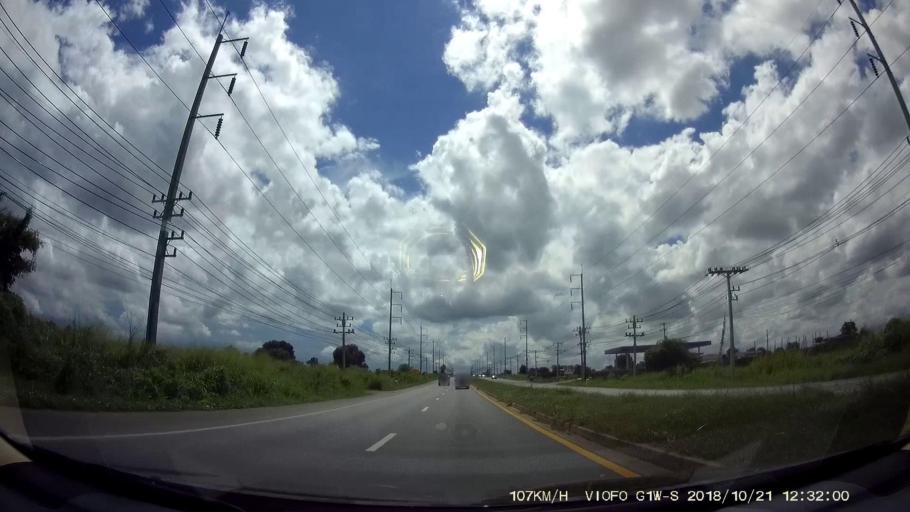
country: TH
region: Nakhon Ratchasima
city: Dan Khun Thot
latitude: 15.1480
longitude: 101.7324
